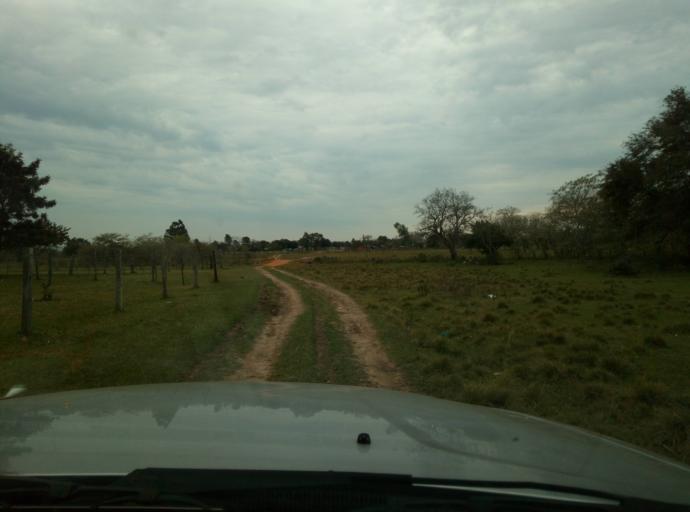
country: PY
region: Caaguazu
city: Carayao
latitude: -25.1600
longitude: -56.3342
